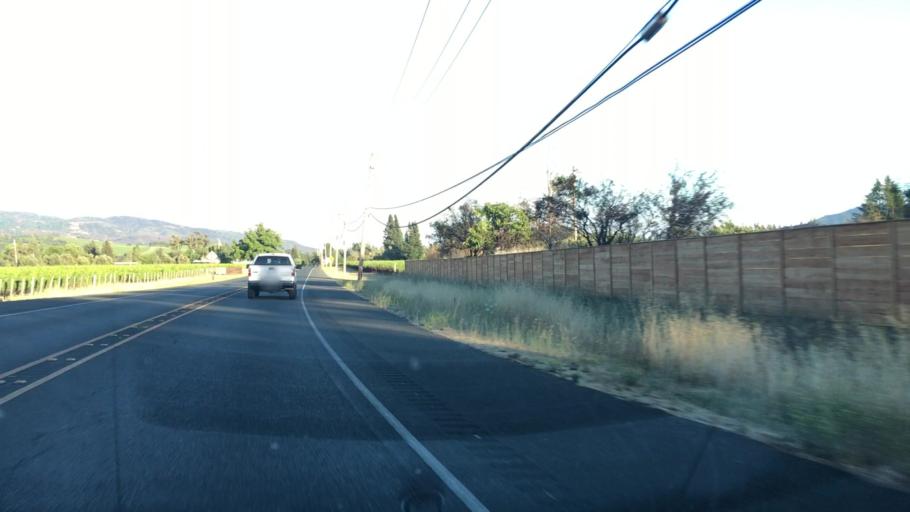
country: US
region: California
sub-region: Sonoma County
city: Kenwood
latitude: 38.4271
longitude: -122.5590
